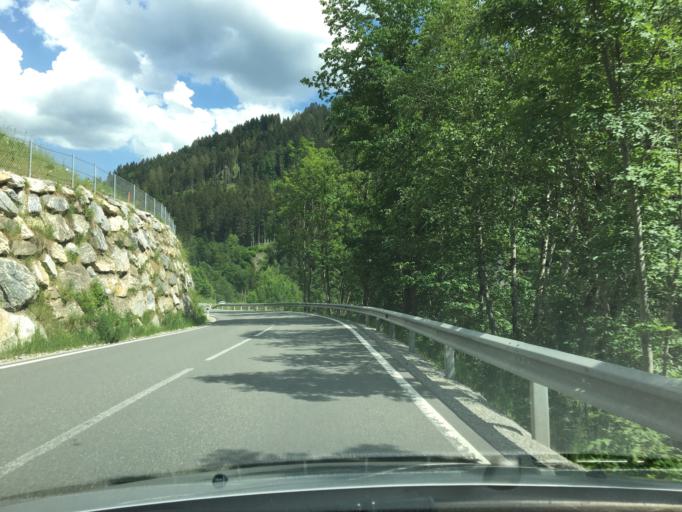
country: AT
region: Salzburg
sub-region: Politischer Bezirk Sankt Johann im Pongau
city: Sankt Johann im Pongau
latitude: 47.3309
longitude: 13.2310
